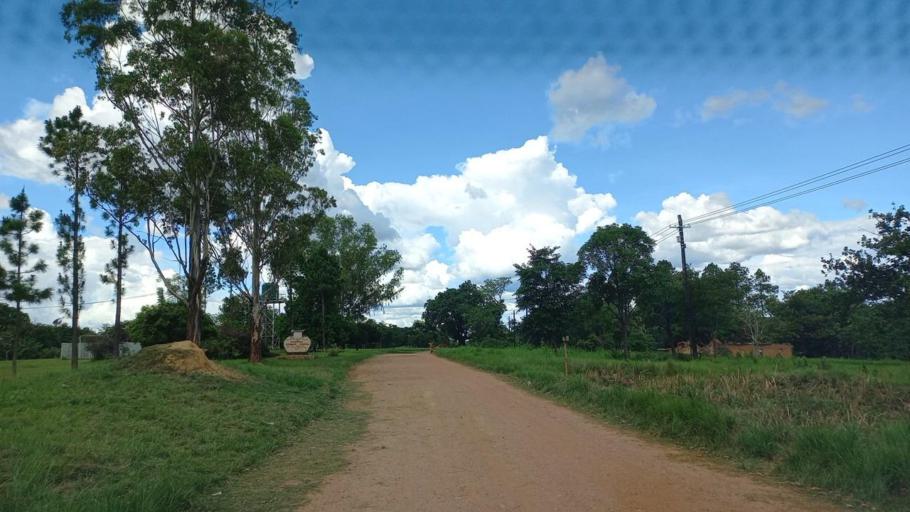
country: ZM
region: North-Western
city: Mwinilunga
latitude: -12.0676
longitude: 24.3019
